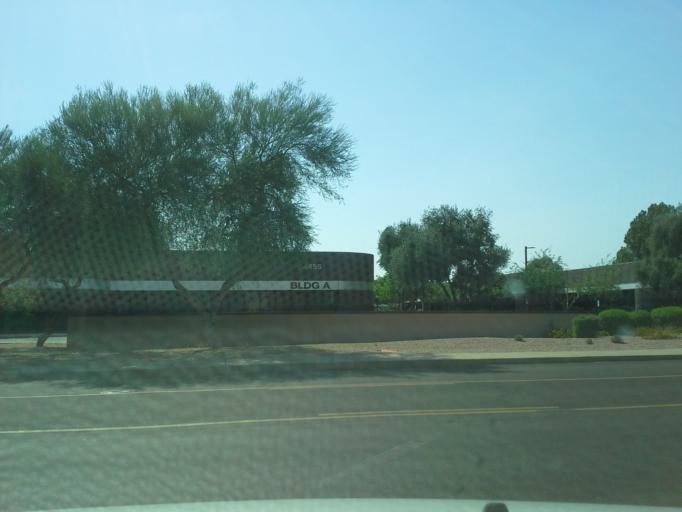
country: US
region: Arizona
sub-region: Maricopa County
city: Paradise Valley
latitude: 33.6172
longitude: -111.9039
